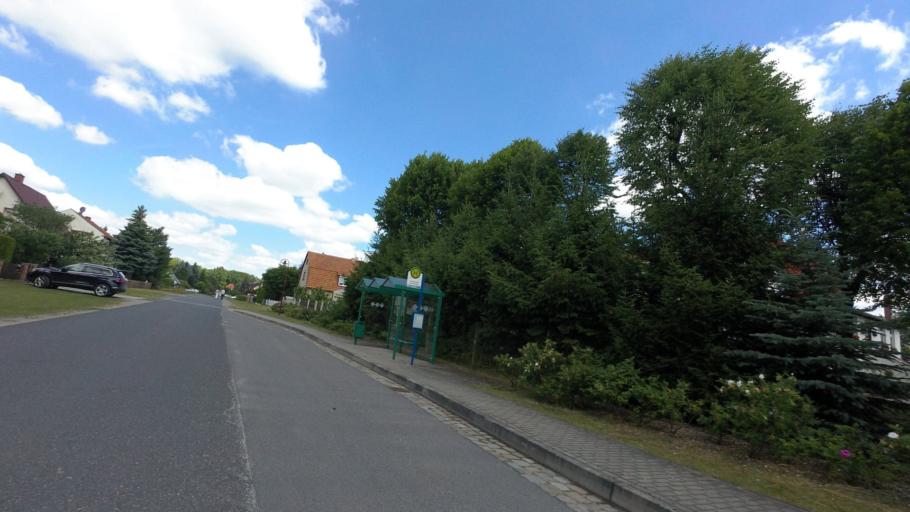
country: DE
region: Brandenburg
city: Finsterwalde
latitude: 51.6392
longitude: 13.6843
